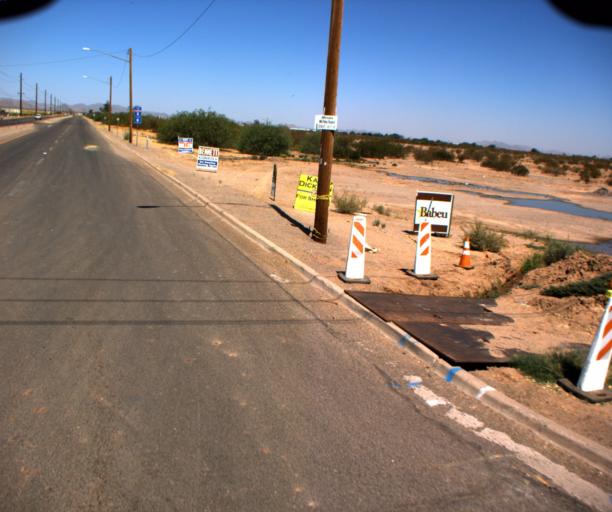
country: US
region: Arizona
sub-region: Pinal County
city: Maricopa
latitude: 32.8795
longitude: -111.9638
